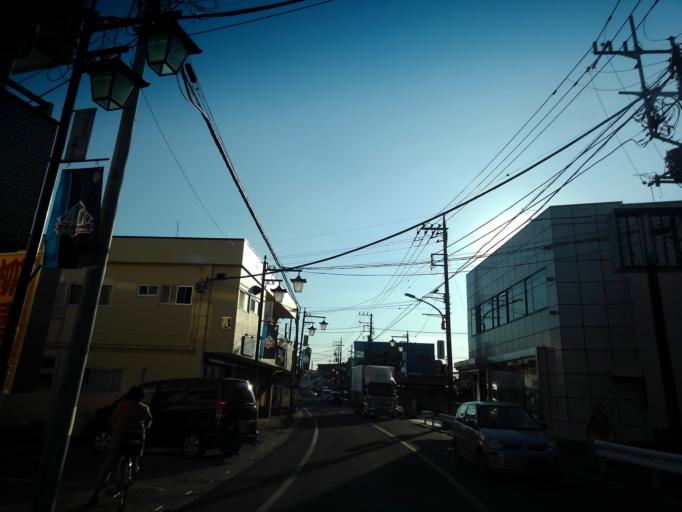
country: JP
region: Saitama
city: Tokorozawa
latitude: 35.7805
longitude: 139.4412
